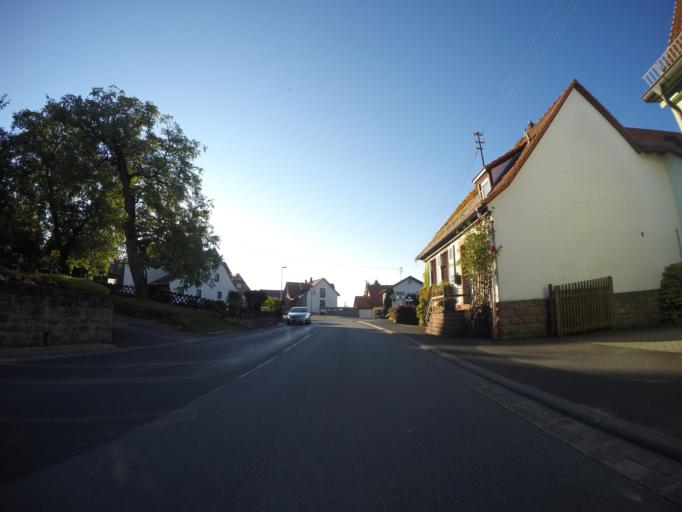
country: DE
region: Bavaria
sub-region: Regierungsbezirk Unterfranken
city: Schollbrunn
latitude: 49.8338
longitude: 9.4664
